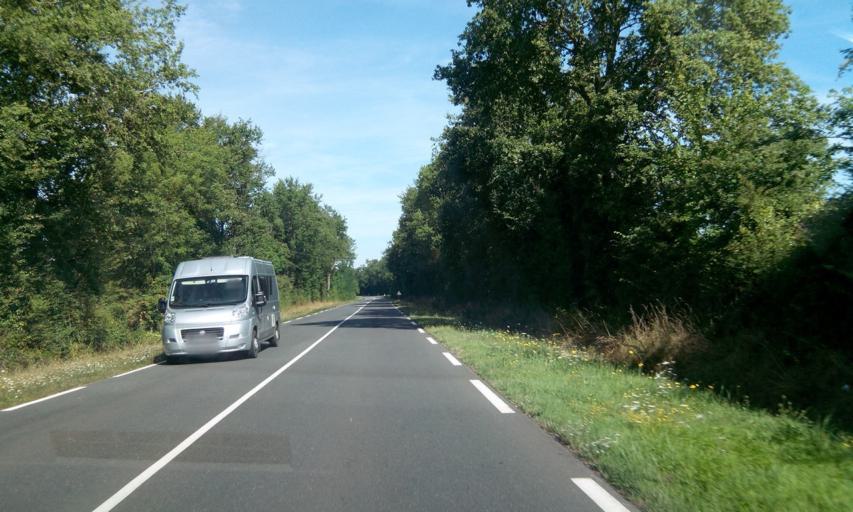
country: FR
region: Poitou-Charentes
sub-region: Departement de la Charente
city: Chabanais
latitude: 45.9433
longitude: 0.7271
